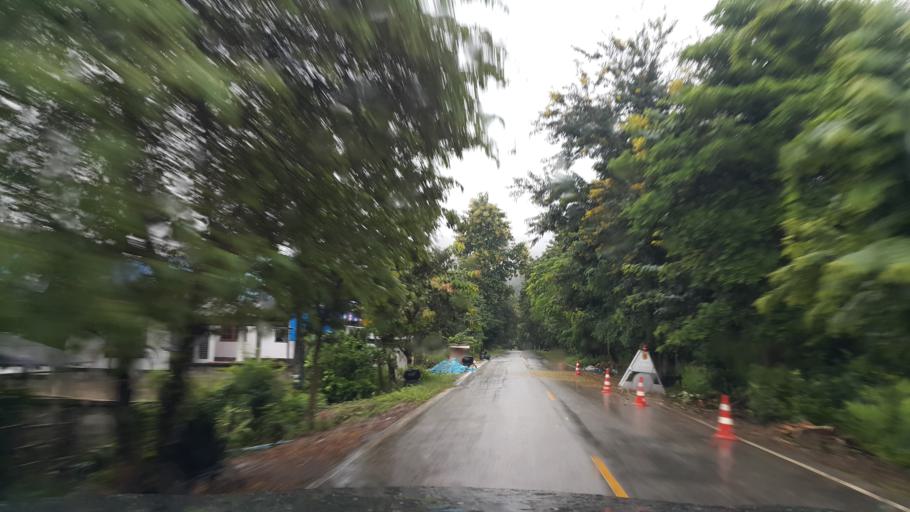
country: TH
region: Phayao
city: Phu Sang
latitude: 19.6052
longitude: 100.4049
